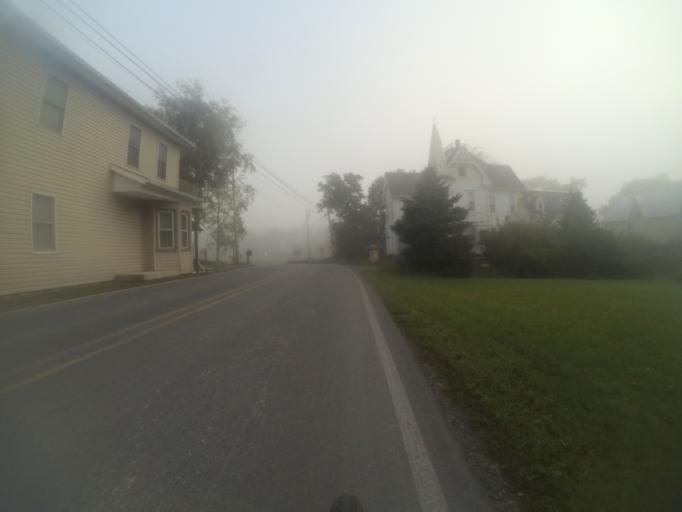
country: US
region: Pennsylvania
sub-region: Mifflin County
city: Milroy
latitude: 40.8688
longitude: -77.4580
